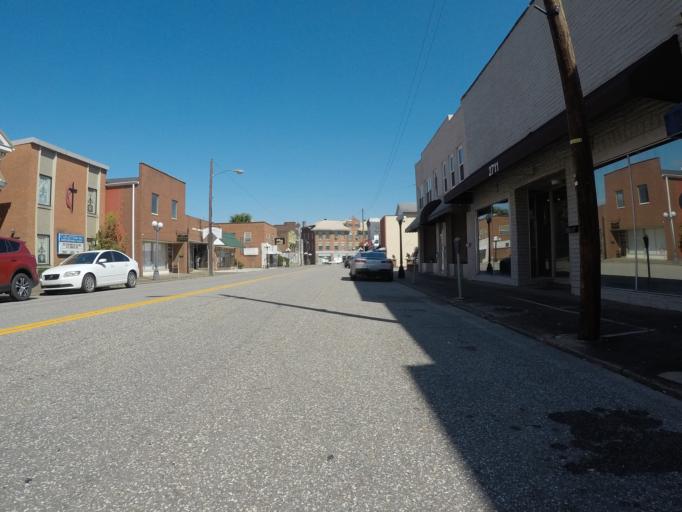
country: US
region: Kentucky
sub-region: Boyd County
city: Catlettsburg
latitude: 38.4160
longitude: -82.5979
